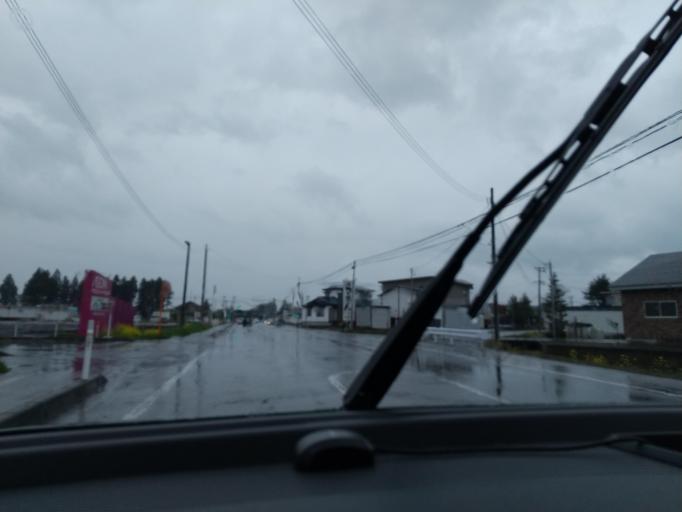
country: JP
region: Akita
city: Omagari
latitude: 39.4153
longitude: 140.5427
